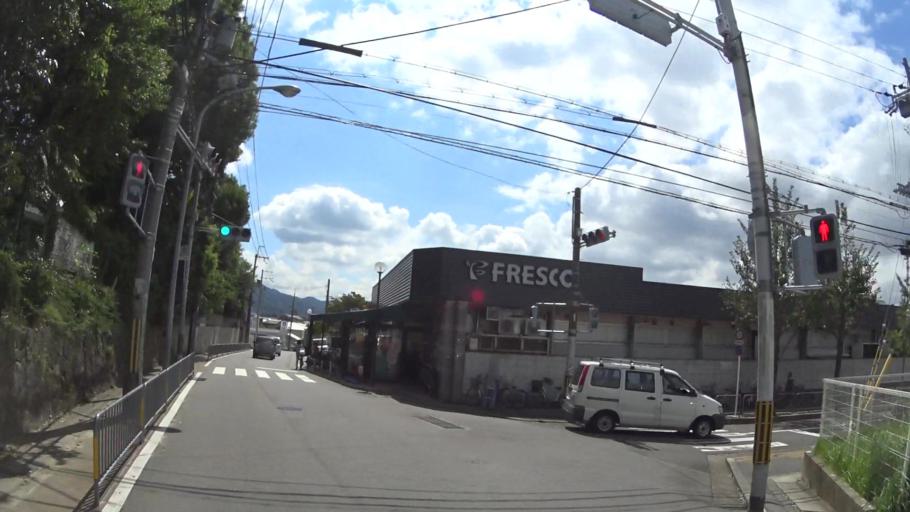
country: JP
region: Shiga Prefecture
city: Otsu-shi
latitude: 34.9698
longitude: 135.8080
